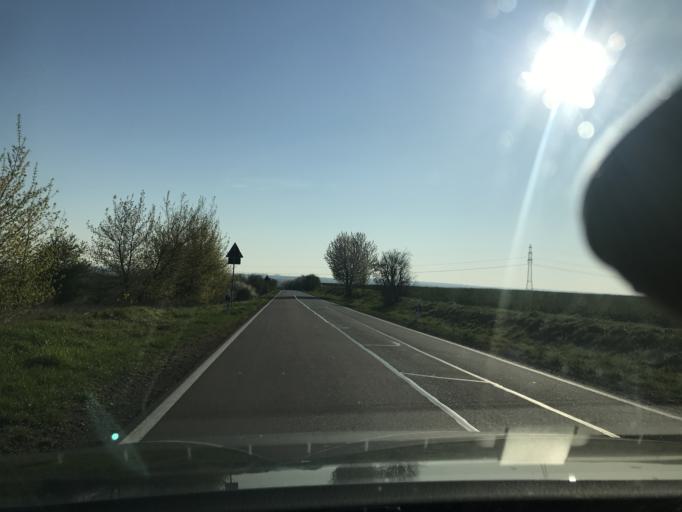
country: DE
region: Saxony-Anhalt
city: Holleben
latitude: 51.4299
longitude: 11.8807
